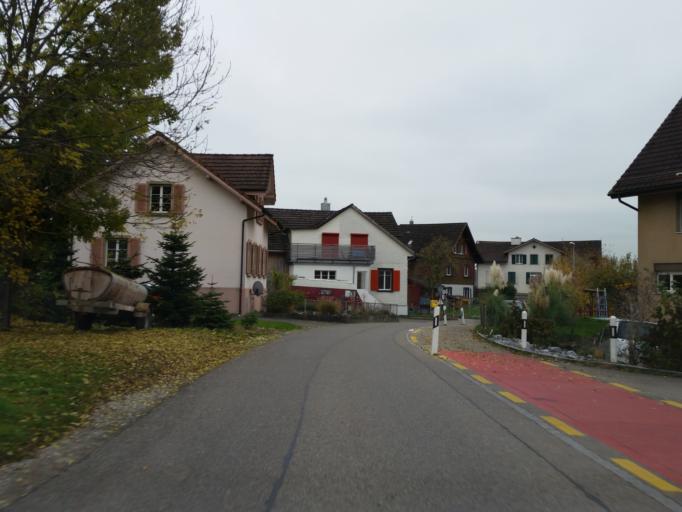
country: CH
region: Thurgau
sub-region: Arbon District
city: Amriswil
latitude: 47.5567
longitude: 9.3240
